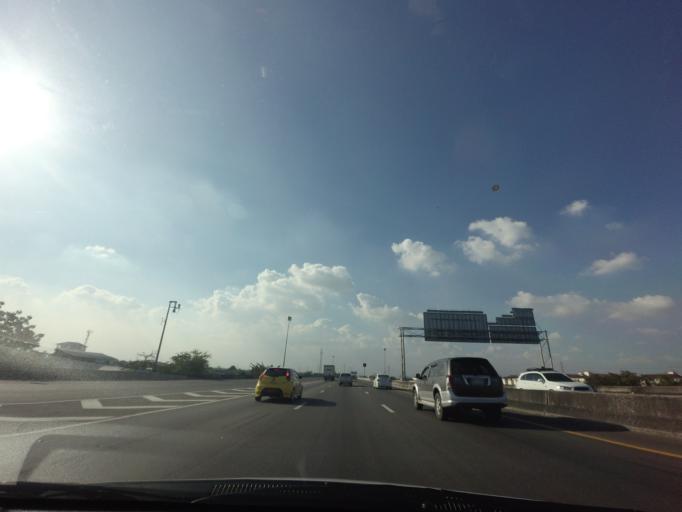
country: TH
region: Samut Prakan
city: Samut Prakan
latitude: 13.6183
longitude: 100.6123
